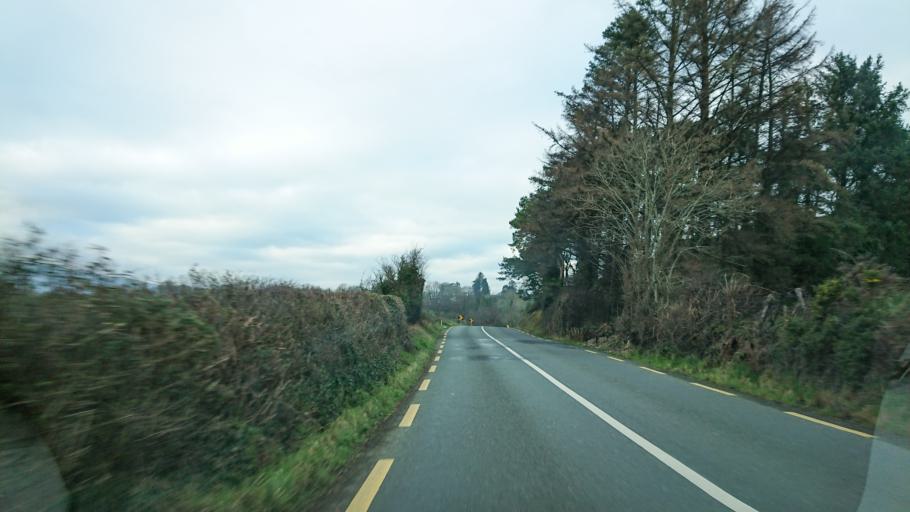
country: IE
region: Munster
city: Carrick-on-Suir
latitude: 52.2992
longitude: -7.4781
